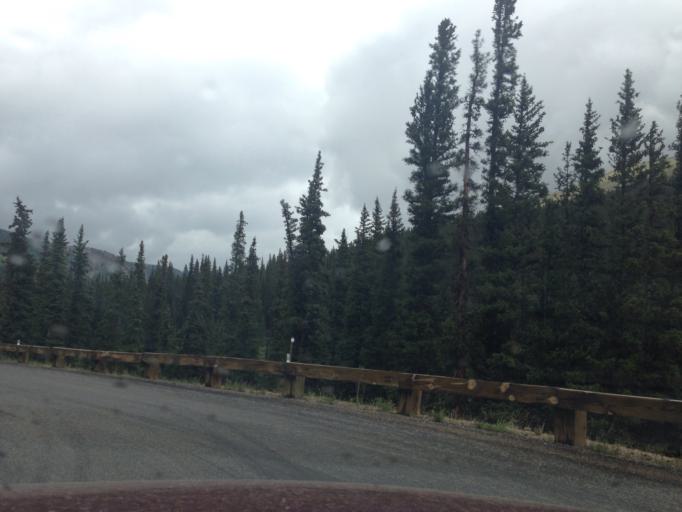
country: US
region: Colorado
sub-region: Clear Creek County
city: Georgetown
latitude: 39.6049
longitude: -105.7113
